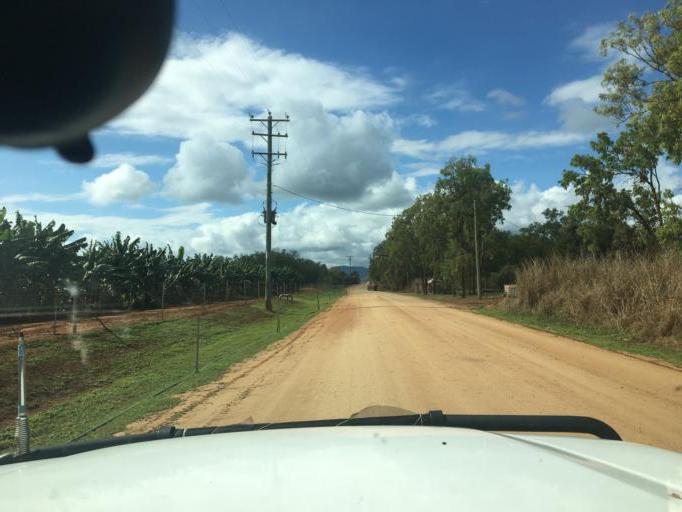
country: AU
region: Queensland
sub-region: Tablelands
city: Mareeba
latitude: -17.0969
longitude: 145.4121
